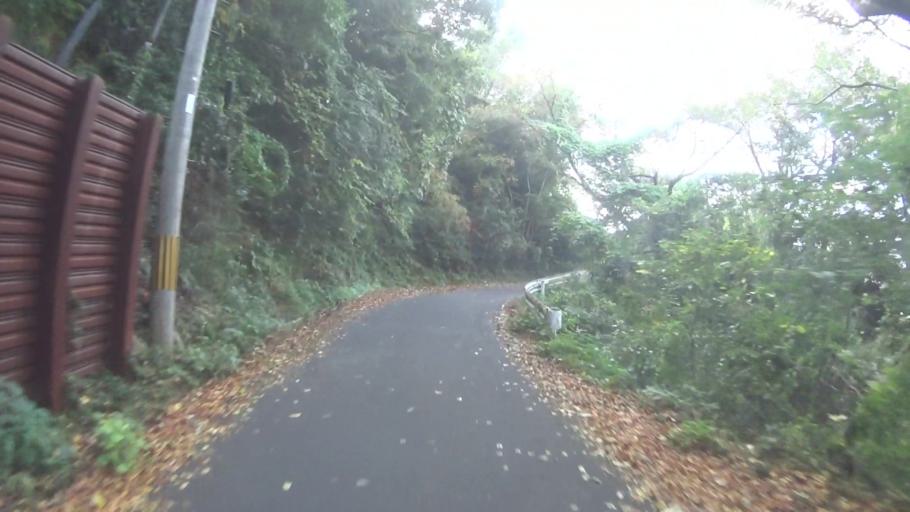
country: JP
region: Kyoto
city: Maizuru
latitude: 35.5677
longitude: 135.4187
